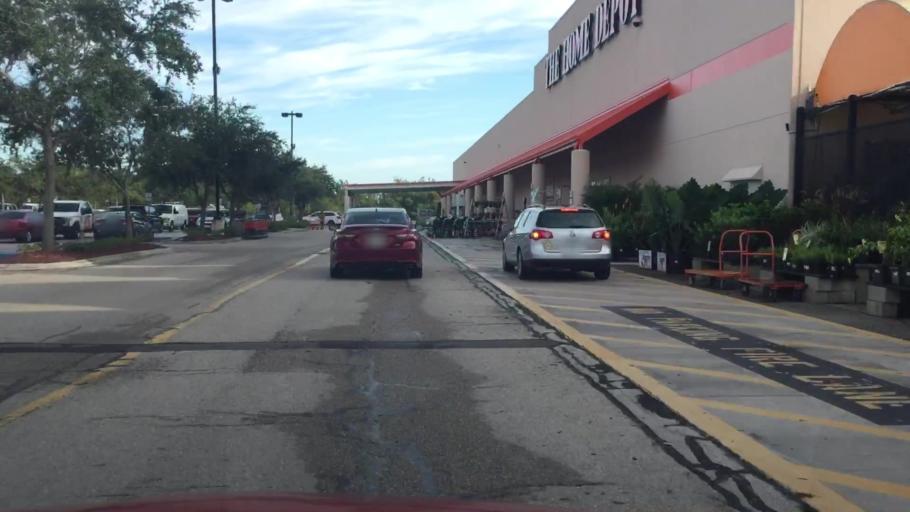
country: US
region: Florida
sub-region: Lee County
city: Villas
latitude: 26.5290
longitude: -81.8682
